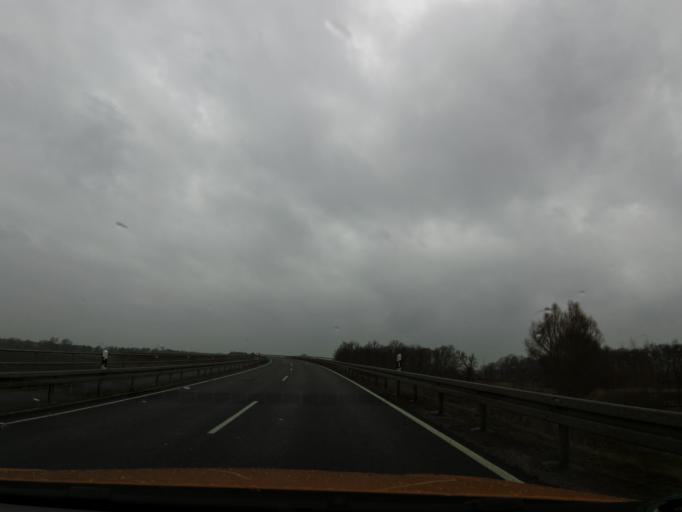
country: DE
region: Brandenburg
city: Roskow
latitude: 52.4094
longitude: 12.6525
